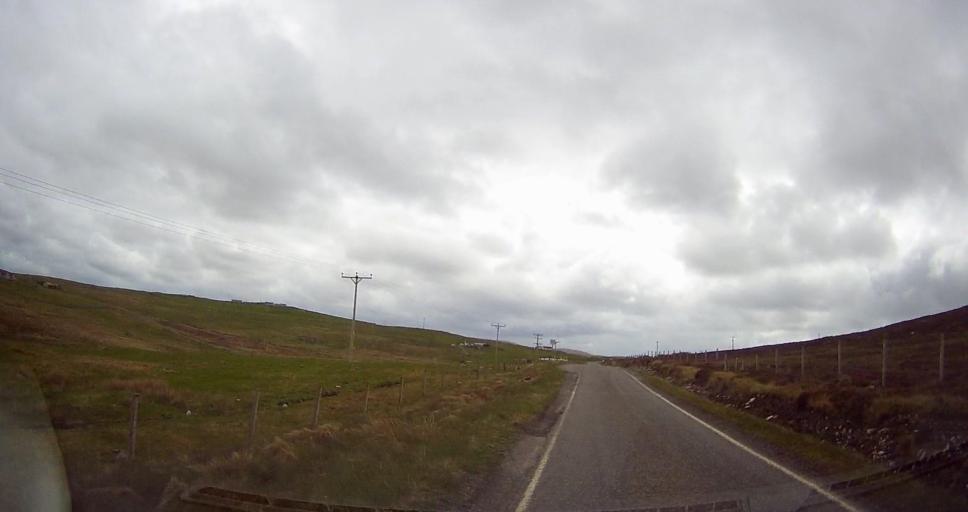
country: GB
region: Scotland
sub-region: Shetland Islands
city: Sandwick
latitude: 60.2465
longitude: -1.5105
